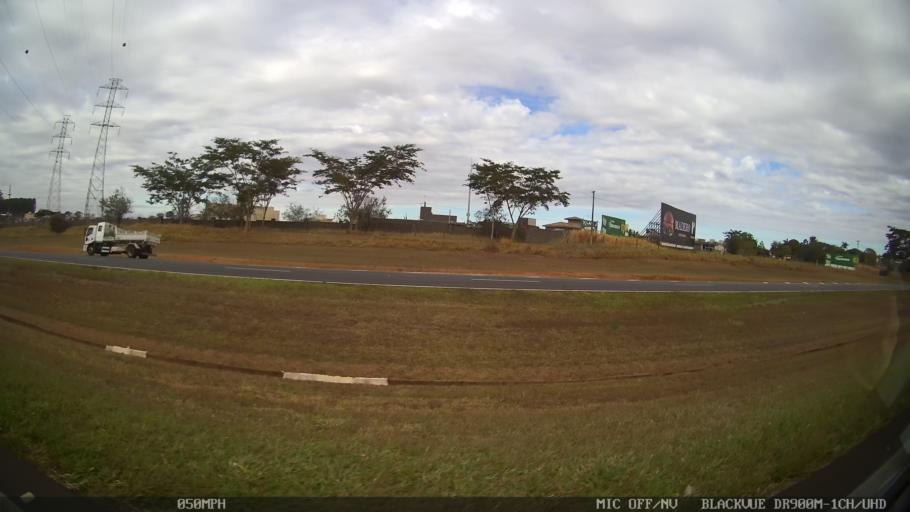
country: BR
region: Sao Paulo
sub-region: Sao Jose Do Rio Preto
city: Sao Jose do Rio Preto
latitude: -20.8154
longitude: -49.4572
